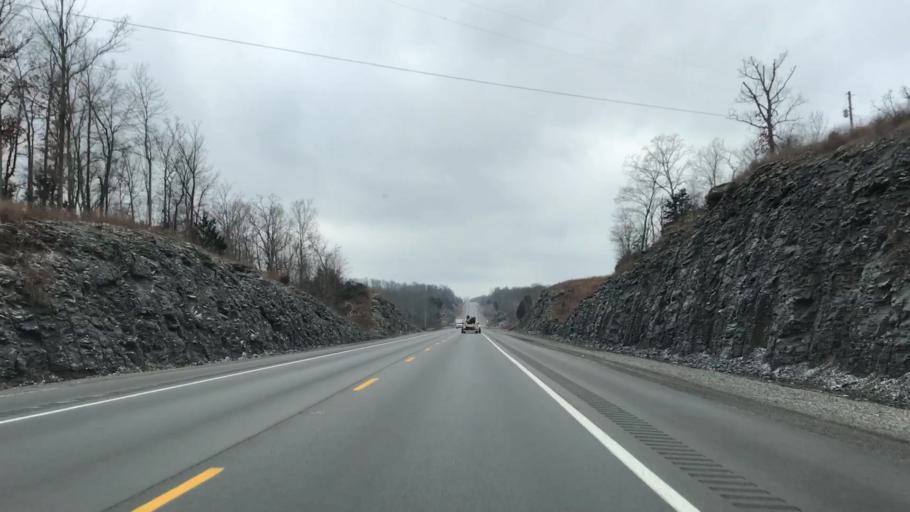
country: US
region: Kentucky
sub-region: Adair County
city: Columbia
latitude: 37.0354
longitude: -85.3761
